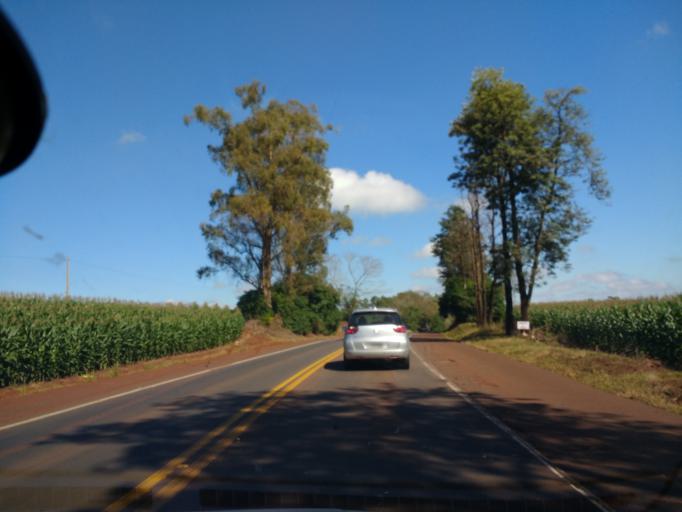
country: BR
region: Parana
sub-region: Cianorte
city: Cianorte
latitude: -23.6517
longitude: -52.4931
